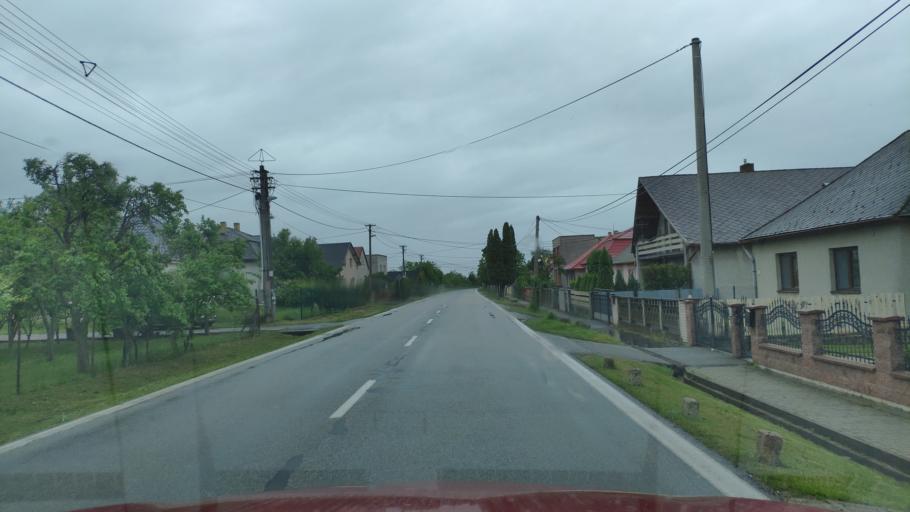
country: HU
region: Borsod-Abauj-Zemplen
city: Satoraljaujhely
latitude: 48.4602
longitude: 21.6428
